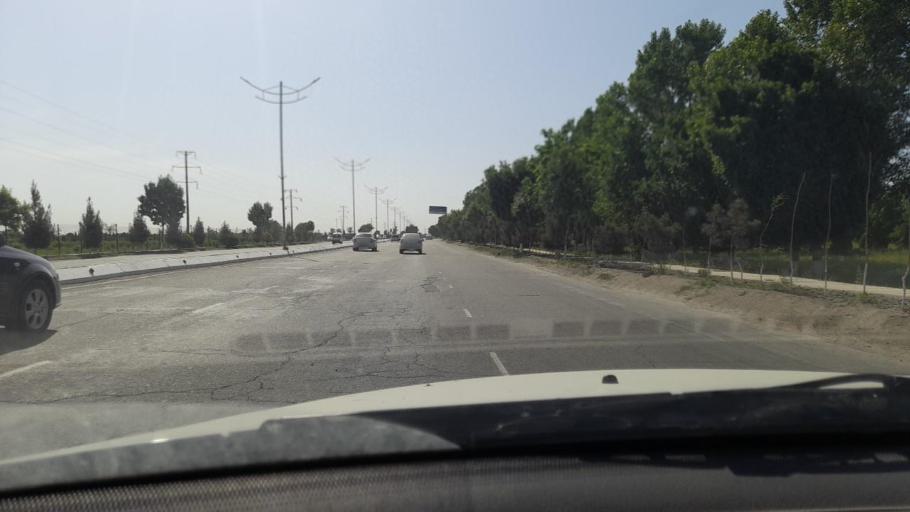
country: UZ
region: Bukhara
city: Bukhara
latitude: 39.8000
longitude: 64.4330
